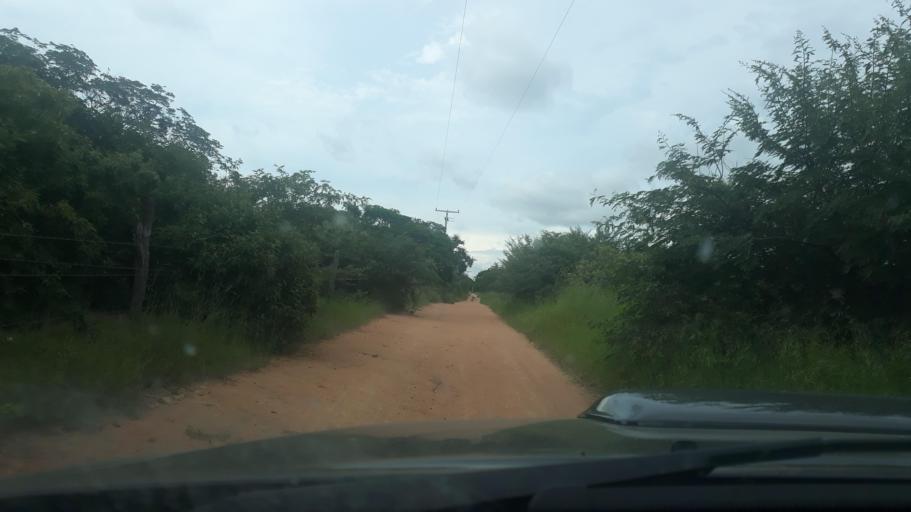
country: BR
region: Bahia
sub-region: Riacho De Santana
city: Riacho de Santana
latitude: -13.8520
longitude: -43.0534
